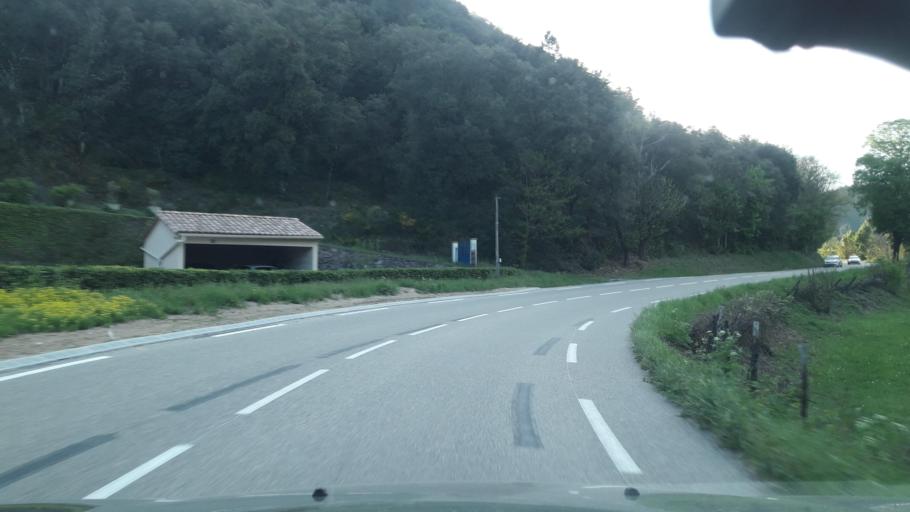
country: FR
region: Languedoc-Roussillon
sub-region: Departement du Gard
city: Lasalle
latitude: 44.1117
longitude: 3.7809
